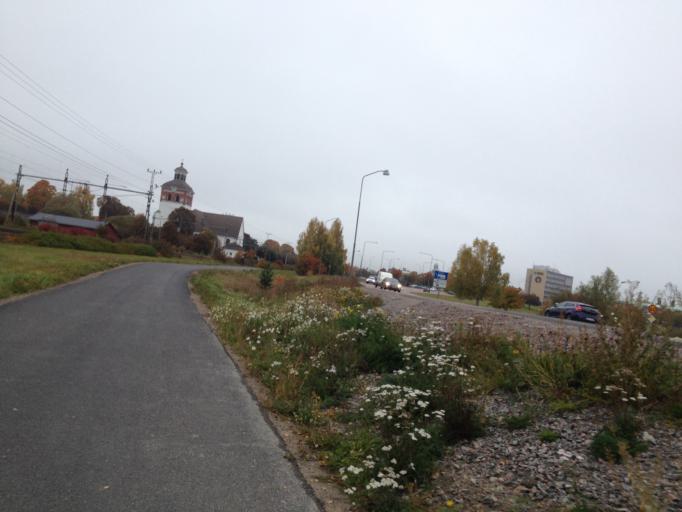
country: SE
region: Gaevleborg
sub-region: Bollnas Kommun
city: Bollnas
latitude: 61.3428
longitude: 16.3913
